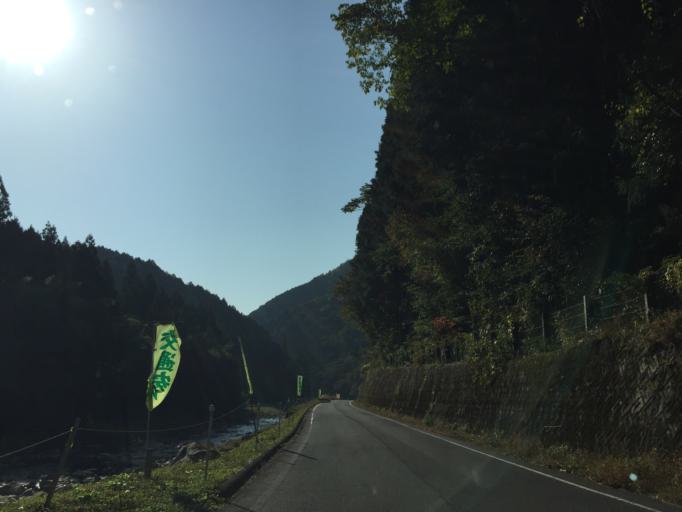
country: JP
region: Gifu
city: Minokamo
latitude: 35.5565
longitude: 137.1152
